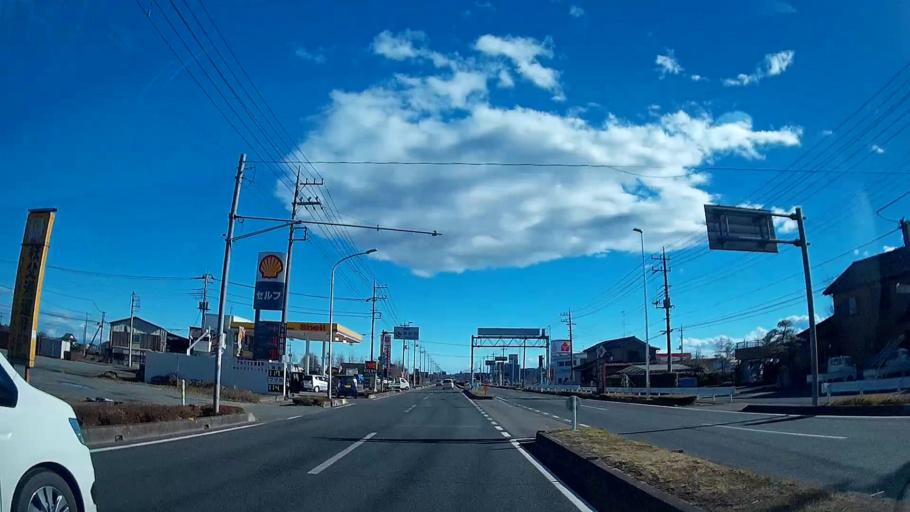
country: JP
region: Saitama
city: Yorii
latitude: 36.1221
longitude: 139.2158
